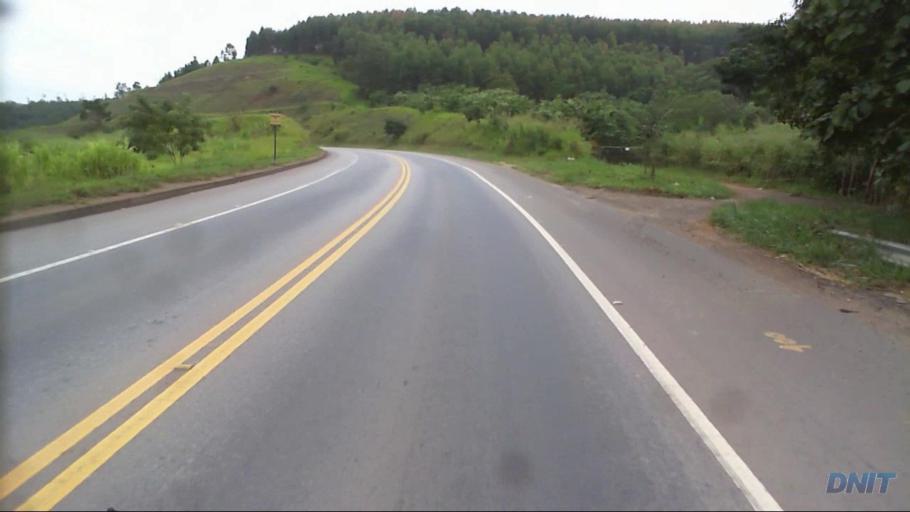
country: BR
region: Minas Gerais
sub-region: Coronel Fabriciano
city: Coronel Fabriciano
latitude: -19.5201
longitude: -42.5809
